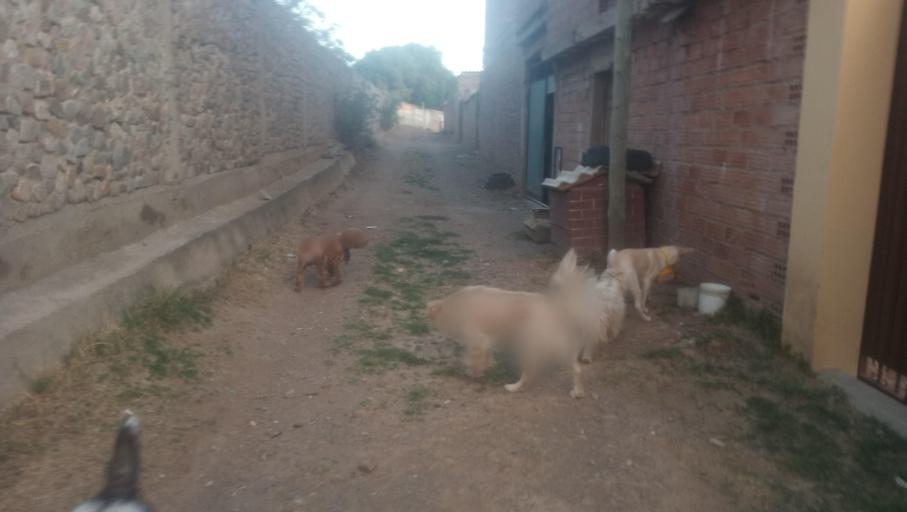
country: BO
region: Cochabamba
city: Cochabamba
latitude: -17.3721
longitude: -66.0941
